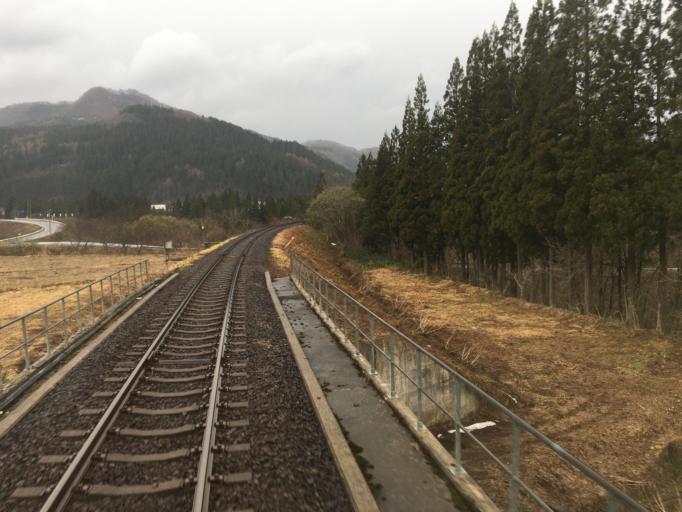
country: JP
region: Akita
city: Kakunodatemachi
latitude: 39.8999
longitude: 140.4631
